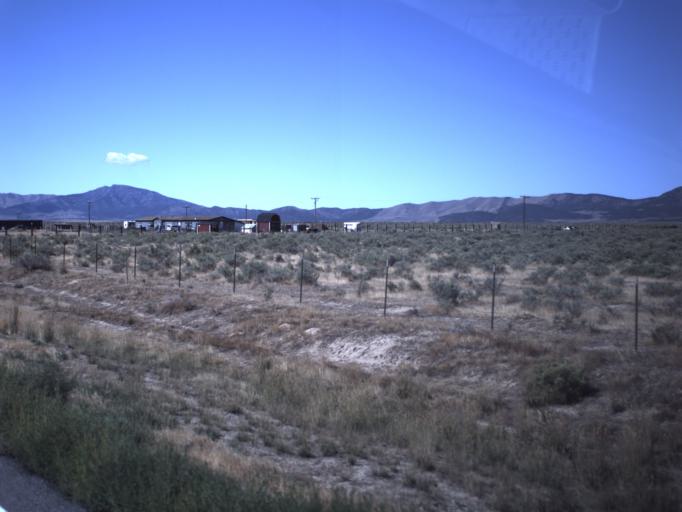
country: US
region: Utah
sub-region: Tooele County
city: Tooele
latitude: 40.1770
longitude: -112.4259
